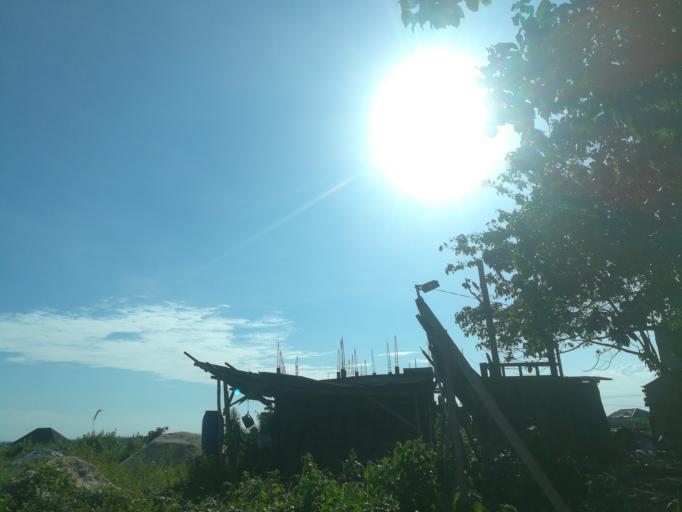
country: NG
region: Lagos
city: Ikorodu
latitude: 6.5639
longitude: 3.5350
